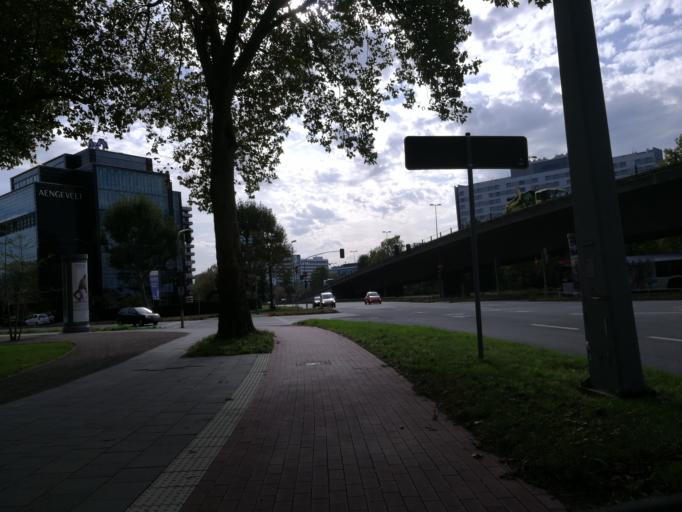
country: DE
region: North Rhine-Westphalia
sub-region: Regierungsbezirk Dusseldorf
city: Dusseldorf
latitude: 51.2524
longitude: 6.7724
